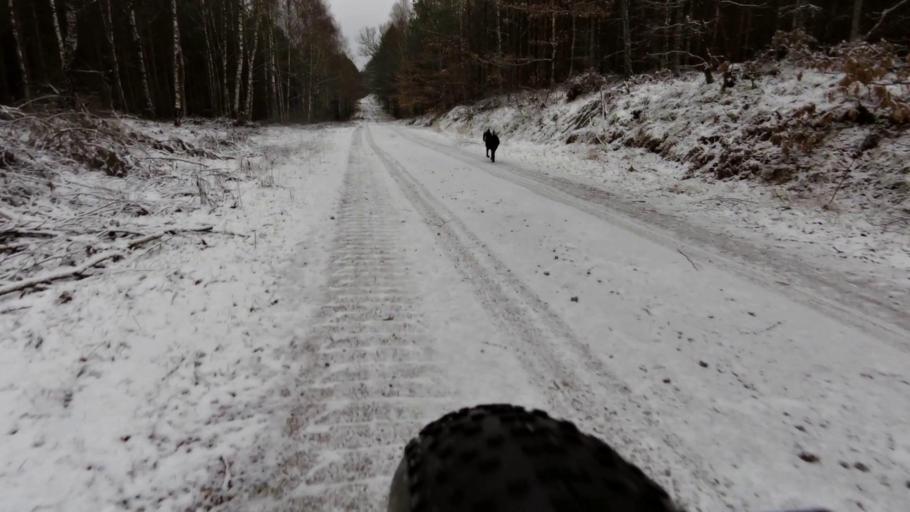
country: PL
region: West Pomeranian Voivodeship
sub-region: Powiat walecki
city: Miroslawiec
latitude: 53.2964
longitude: 16.0588
